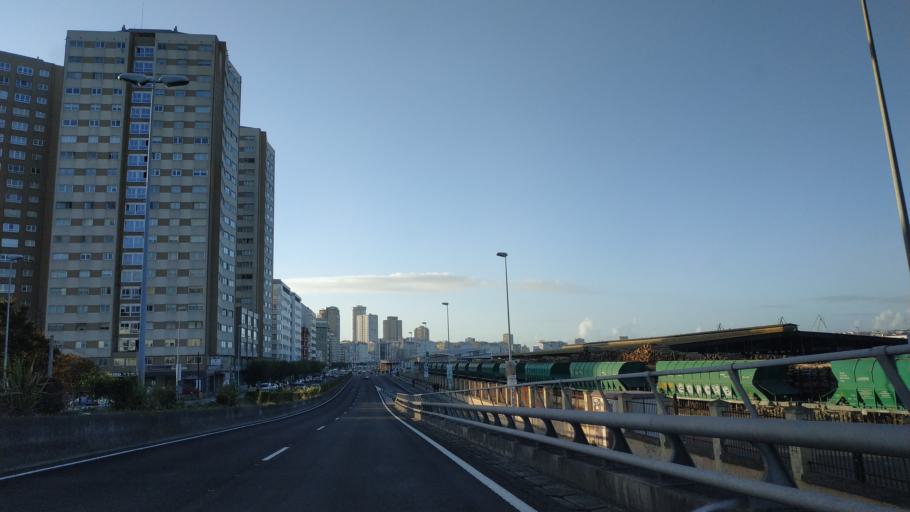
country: ES
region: Galicia
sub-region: Provincia da Coruna
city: A Coruna
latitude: 43.3558
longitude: -8.3967
